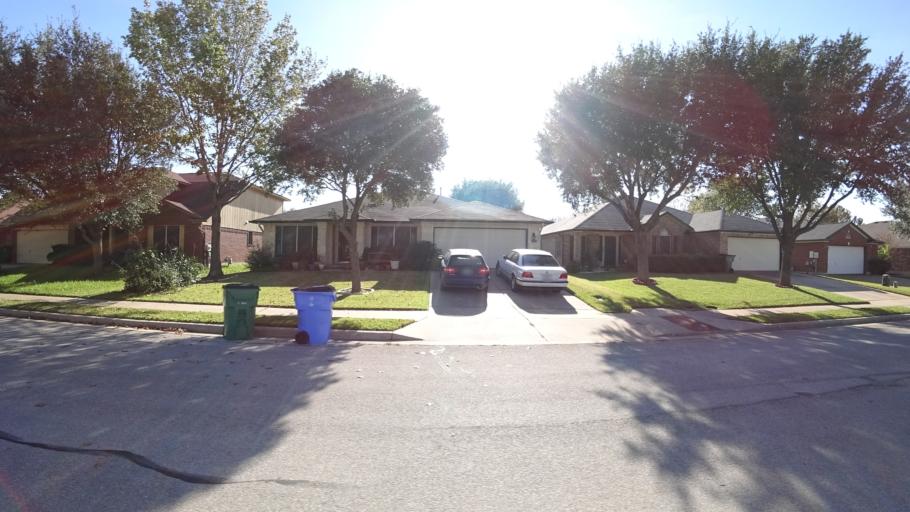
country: US
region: Texas
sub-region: Travis County
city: Wells Branch
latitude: 30.4629
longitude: -97.6888
